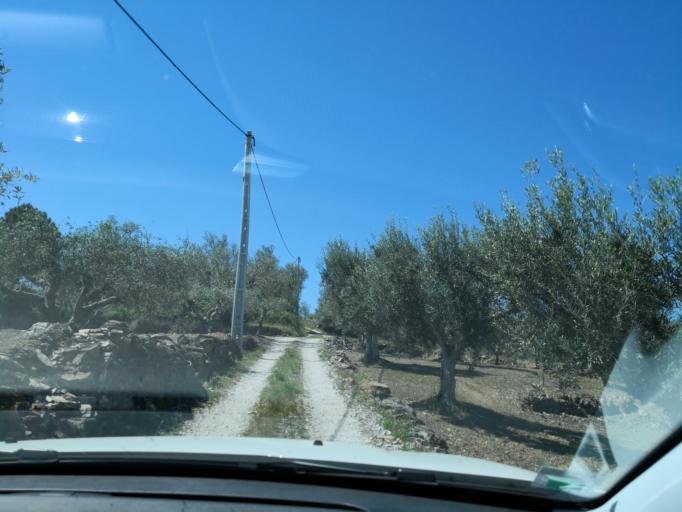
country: PT
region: Vila Real
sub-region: Vila Real
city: Vila Real
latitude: 41.2417
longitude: -7.7210
